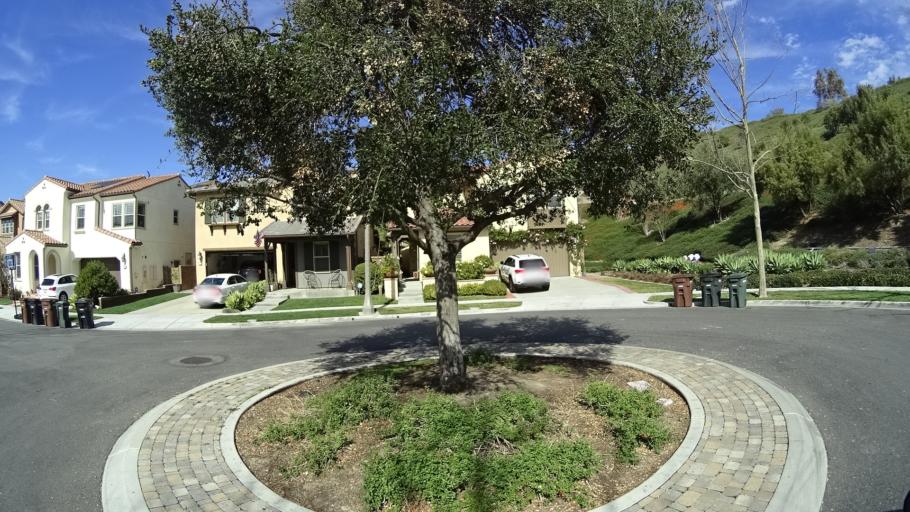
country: US
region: California
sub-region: Orange County
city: Ladera Ranch
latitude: 33.5268
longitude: -117.6198
